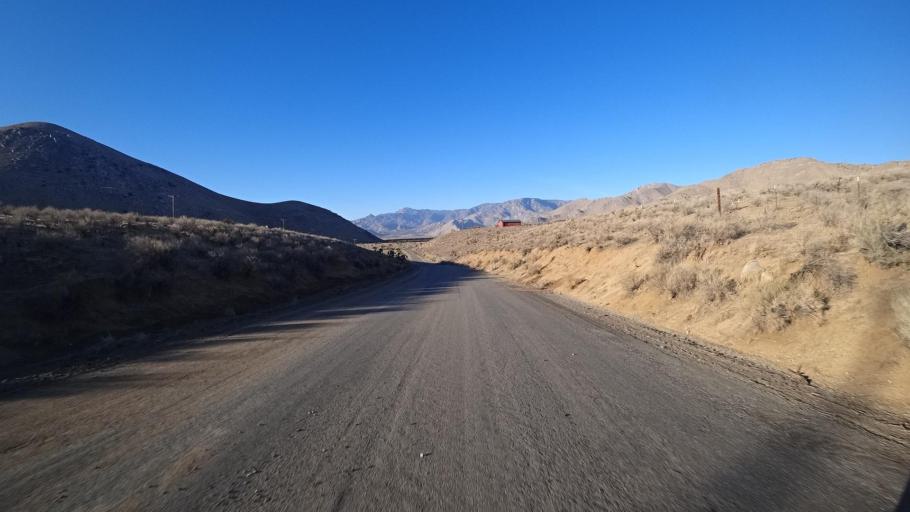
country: US
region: California
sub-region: Kern County
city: Weldon
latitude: 35.6038
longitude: -118.2424
